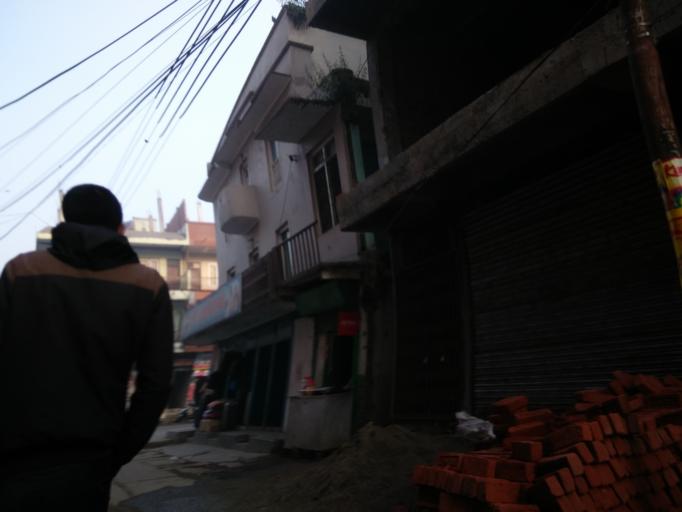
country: NP
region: Central Region
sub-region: Narayani Zone
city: Bharatpur
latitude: 27.6984
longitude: 84.4240
